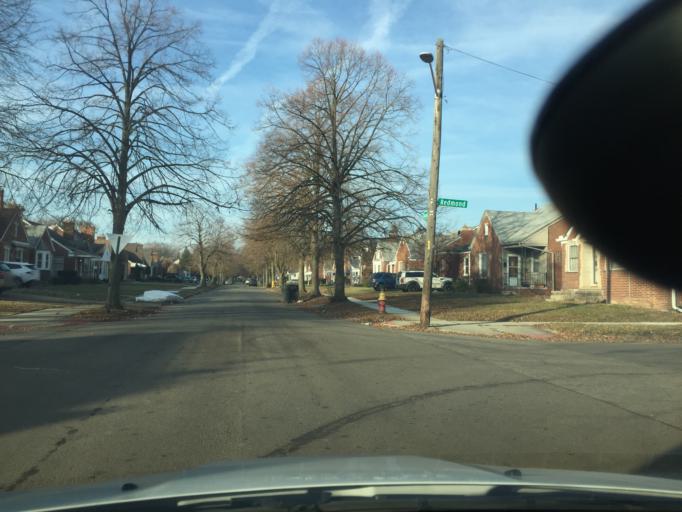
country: US
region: Michigan
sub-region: Wayne County
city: Harper Woods
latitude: 42.4332
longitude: -82.9556
